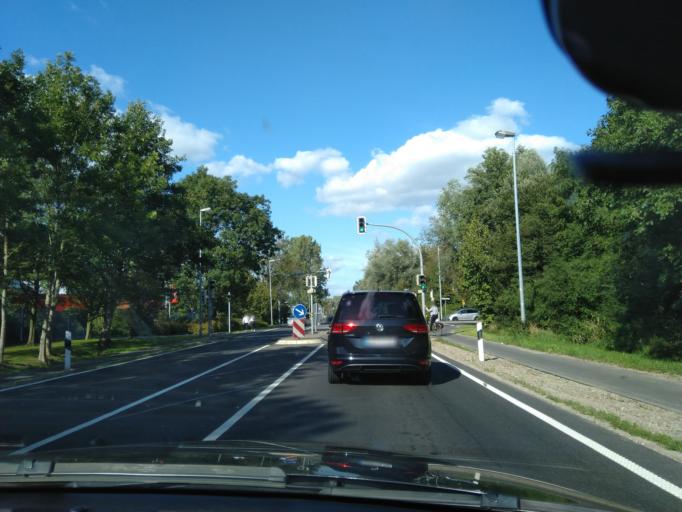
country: DE
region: Lower Saxony
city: Leer
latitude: 53.2556
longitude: 7.4580
